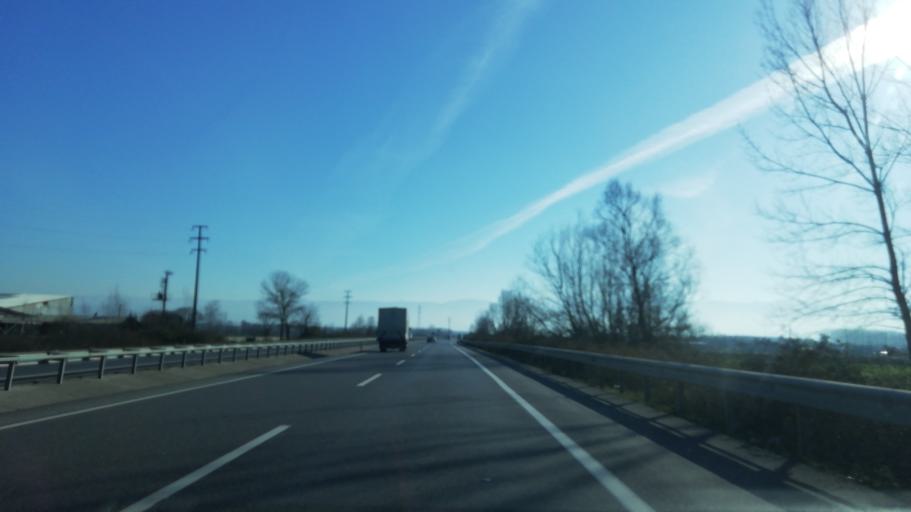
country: TR
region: Sakarya
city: Akyazi
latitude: 40.7386
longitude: 30.5646
